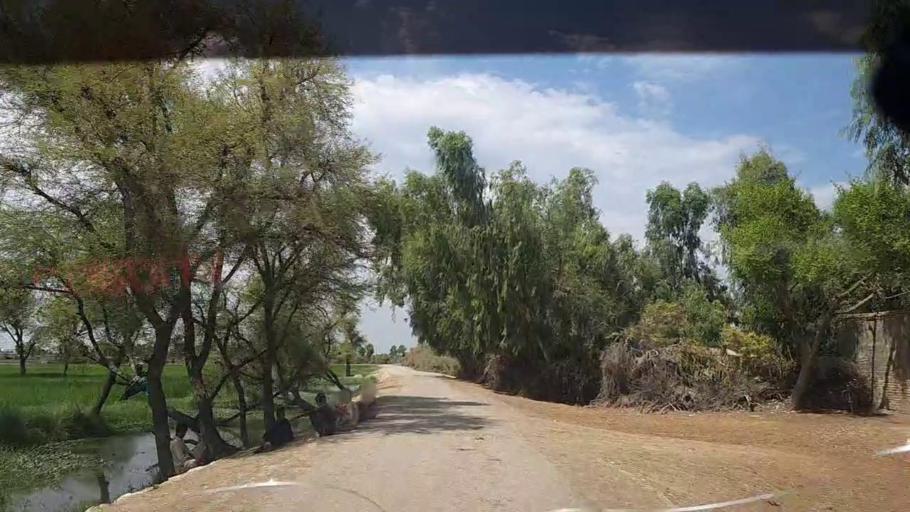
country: PK
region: Sindh
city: Ghauspur
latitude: 28.1521
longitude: 68.9975
